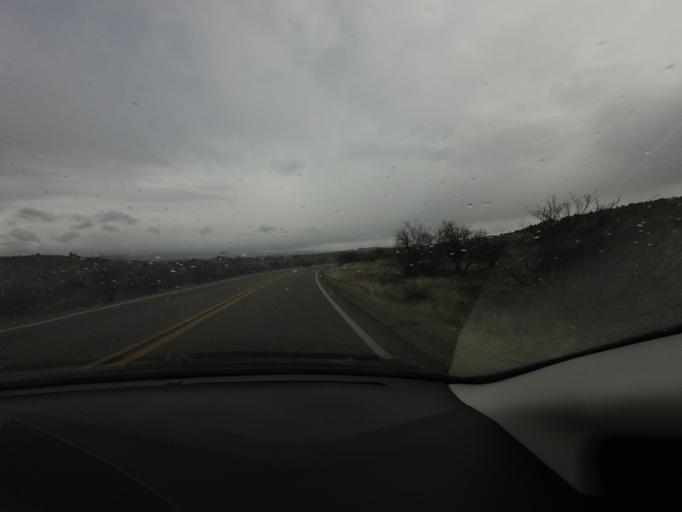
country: US
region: Arizona
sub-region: Yavapai County
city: Lake Montezuma
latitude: 34.6612
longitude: -111.8227
